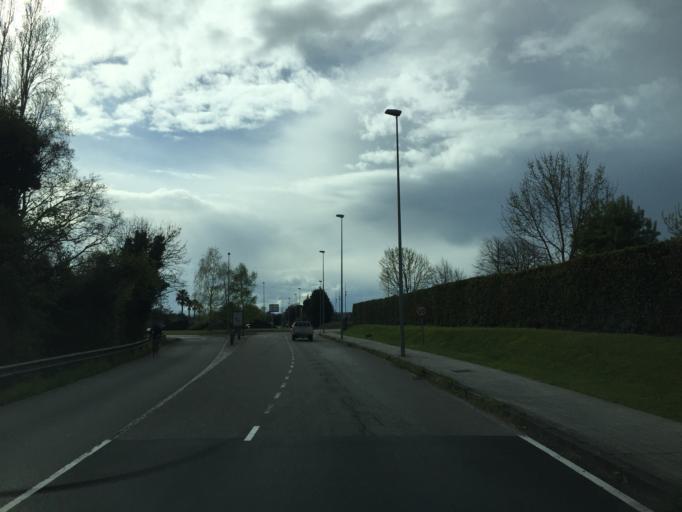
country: ES
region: Asturias
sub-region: Province of Asturias
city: Gijon
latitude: 43.5217
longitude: -5.6126
